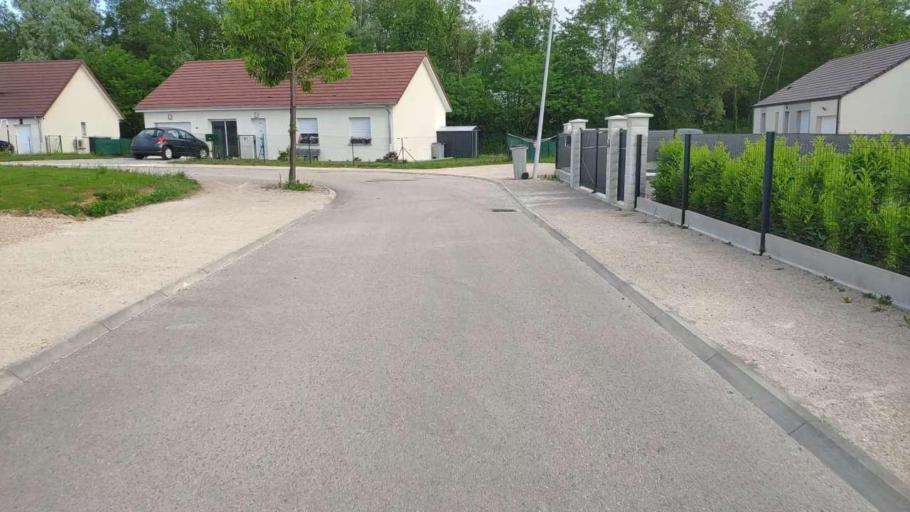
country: FR
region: Franche-Comte
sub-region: Departement du Jura
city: Bletterans
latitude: 46.7518
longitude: 5.4445
